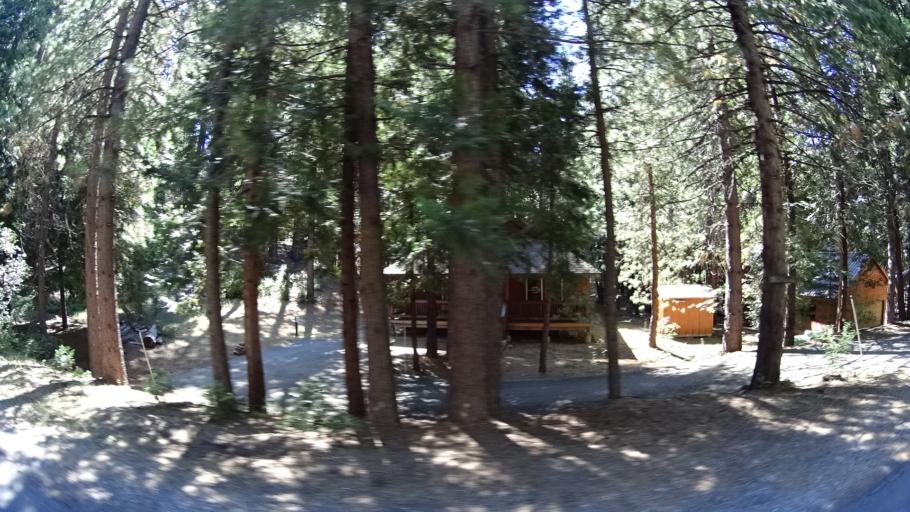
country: US
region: California
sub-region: Calaveras County
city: Arnold
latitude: 38.2817
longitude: -120.2772
